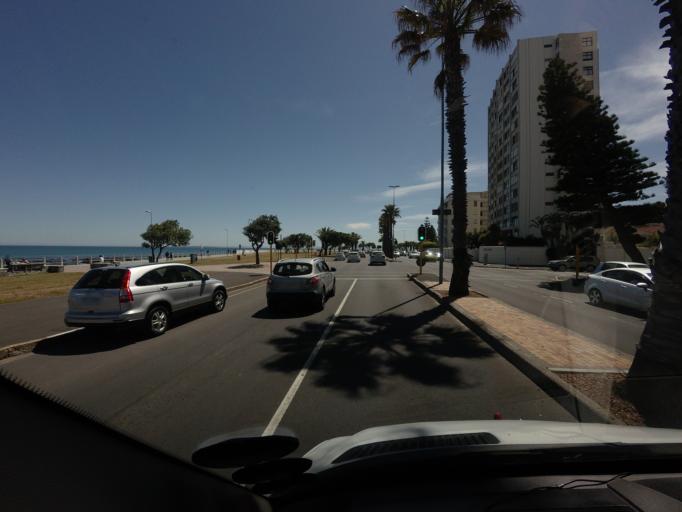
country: ZA
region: Western Cape
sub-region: City of Cape Town
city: Cape Town
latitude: -33.9124
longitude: 18.3886
